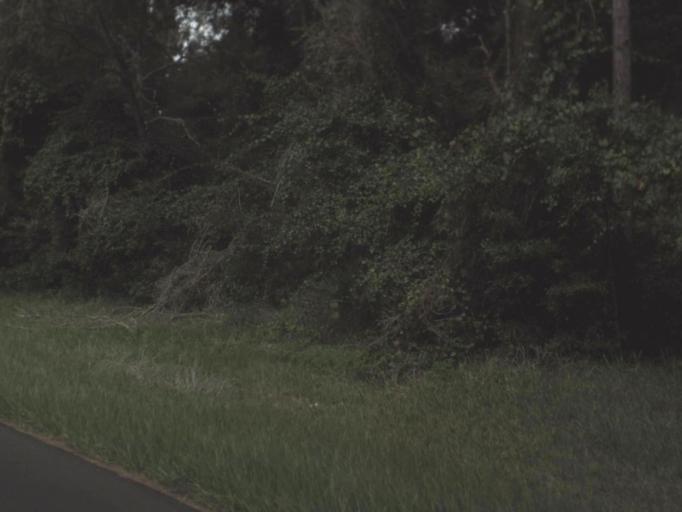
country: US
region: Florida
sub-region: Citrus County
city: Floral City
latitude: 28.6901
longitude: -82.3189
